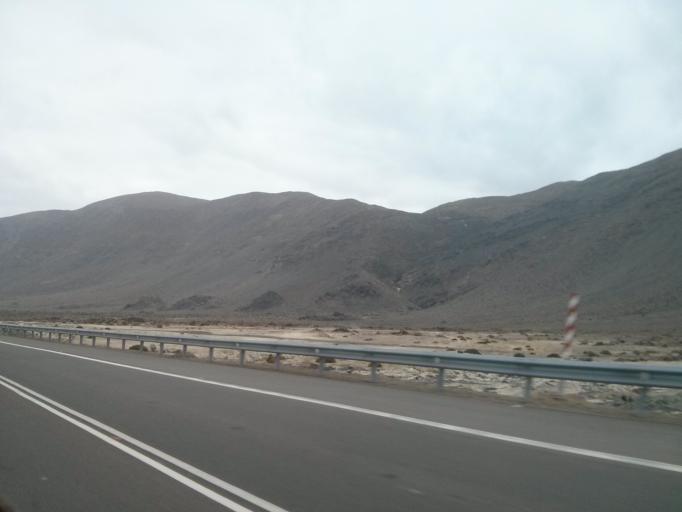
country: CL
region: Atacama
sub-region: Provincia de Chanaral
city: Diego de Almagro
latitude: -26.4524
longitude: -70.6816
